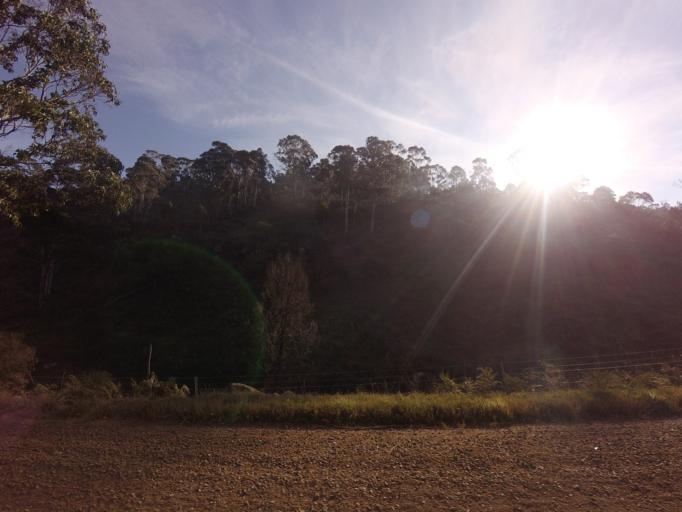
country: AU
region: Tasmania
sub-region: Brighton
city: Bridgewater
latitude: -42.5074
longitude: 147.4284
